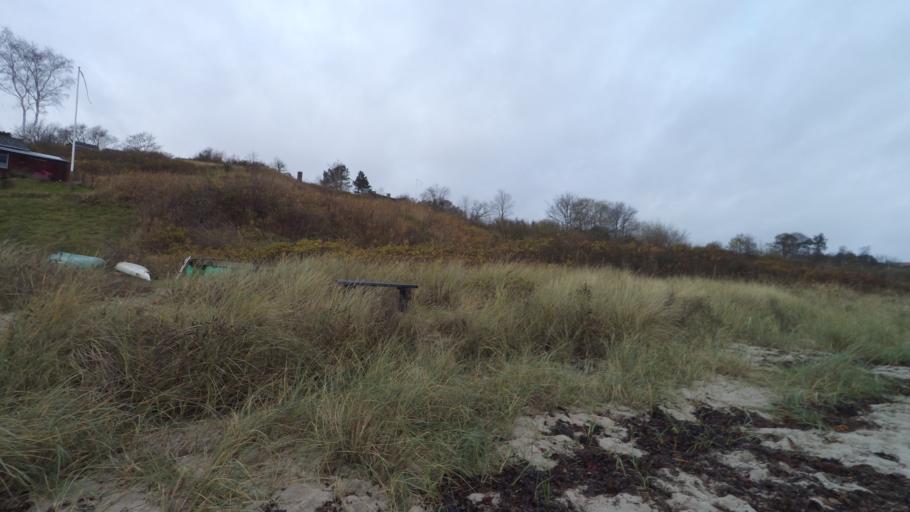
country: DK
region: Central Jutland
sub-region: Arhus Kommune
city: Malling
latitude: 55.9935
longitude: 10.2539
